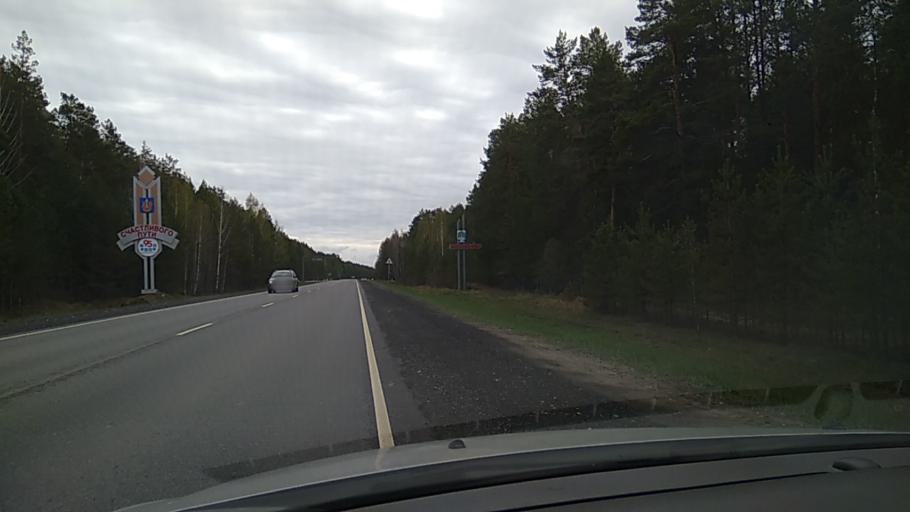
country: RU
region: Tjumen
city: Chervishevo
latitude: 56.8185
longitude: 65.3802
